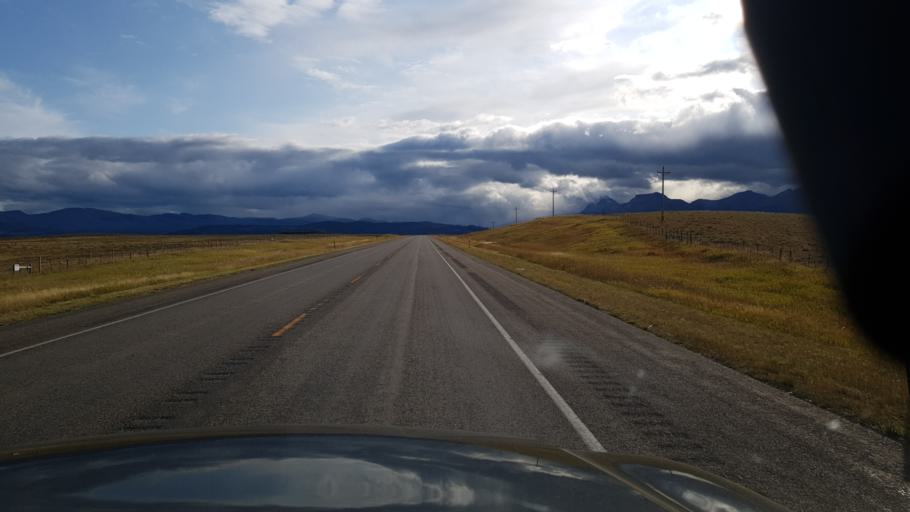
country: US
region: Montana
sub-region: Glacier County
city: South Browning
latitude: 48.4750
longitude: -113.1452
